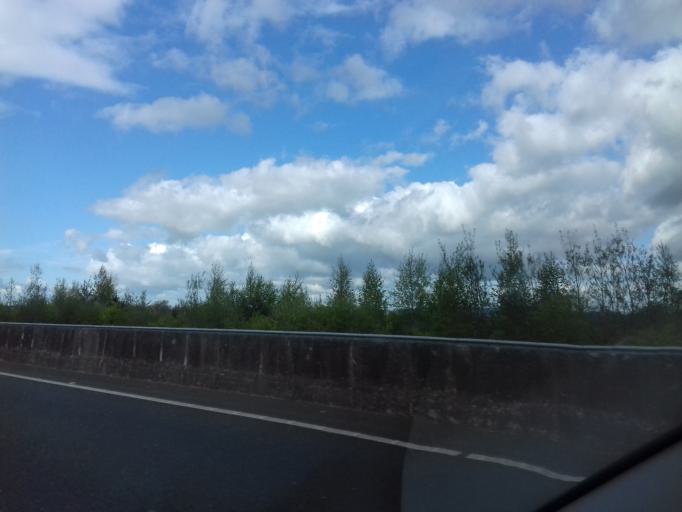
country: IE
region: Leinster
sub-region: Kilkenny
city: Thomastown
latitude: 52.4850
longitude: -7.2407
